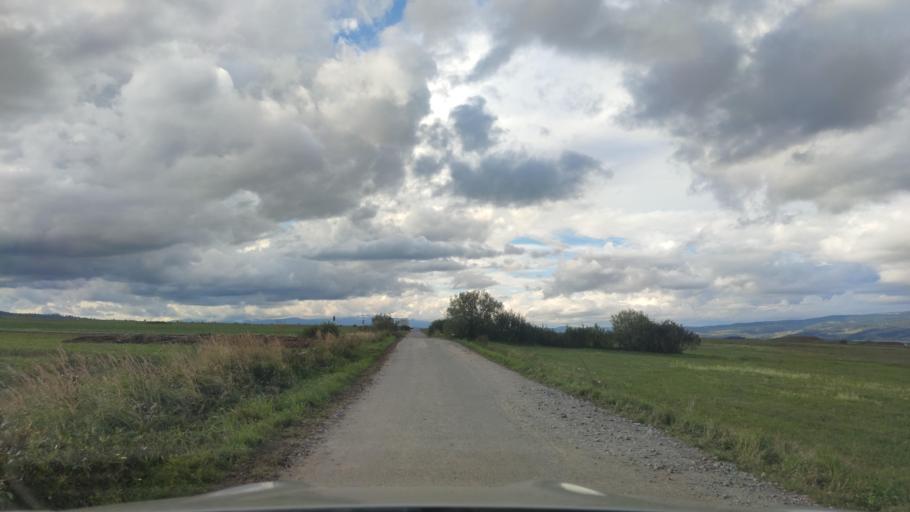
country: RO
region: Harghita
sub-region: Comuna Remetea
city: Remetea
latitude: 46.8154
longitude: 25.4347
